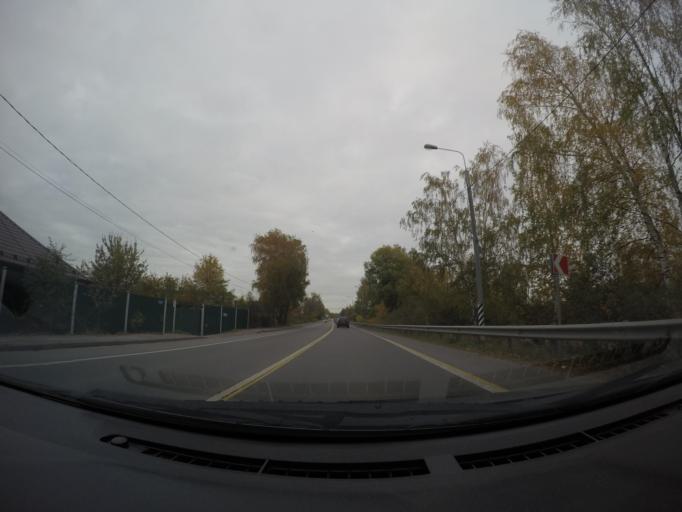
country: RU
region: Moskovskaya
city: Elektrougli
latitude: 55.7252
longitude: 38.2535
